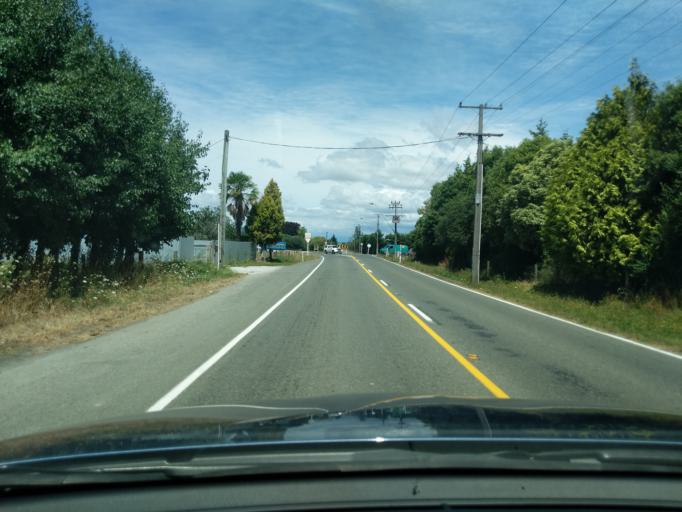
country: NZ
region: Tasman
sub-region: Tasman District
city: Motueka
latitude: -41.0896
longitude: 172.9967
